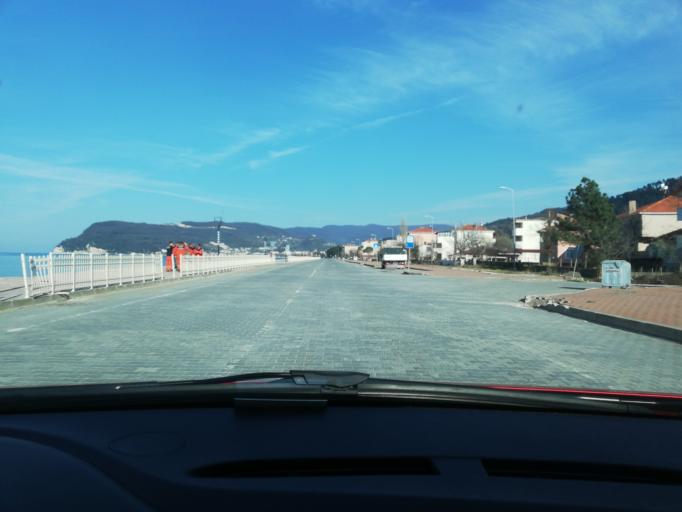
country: TR
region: Kastamonu
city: Cide
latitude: 41.8856
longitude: 32.9562
